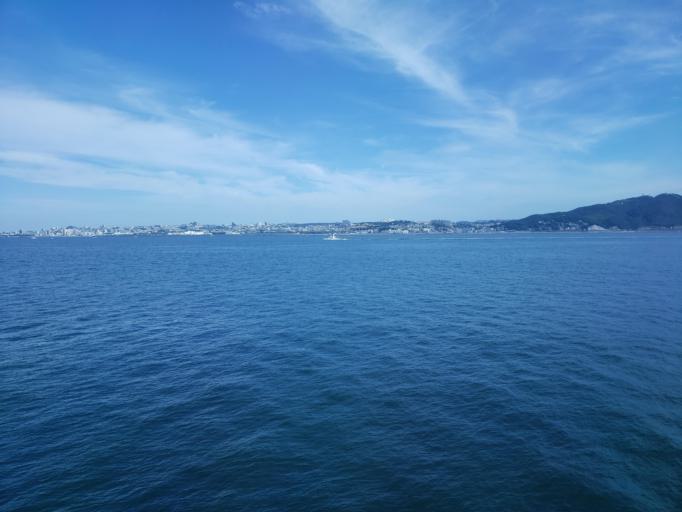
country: JP
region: Hyogo
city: Akashi
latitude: 34.6035
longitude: 135.0881
